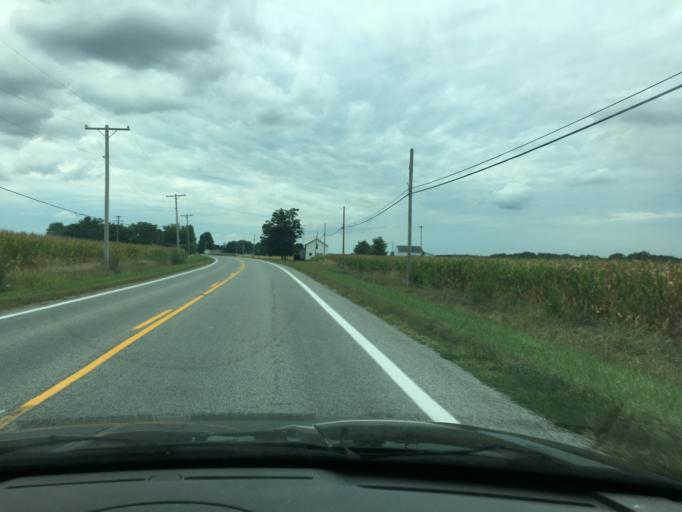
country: US
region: Ohio
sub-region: Champaign County
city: Urbana
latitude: 40.1548
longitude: -83.7342
